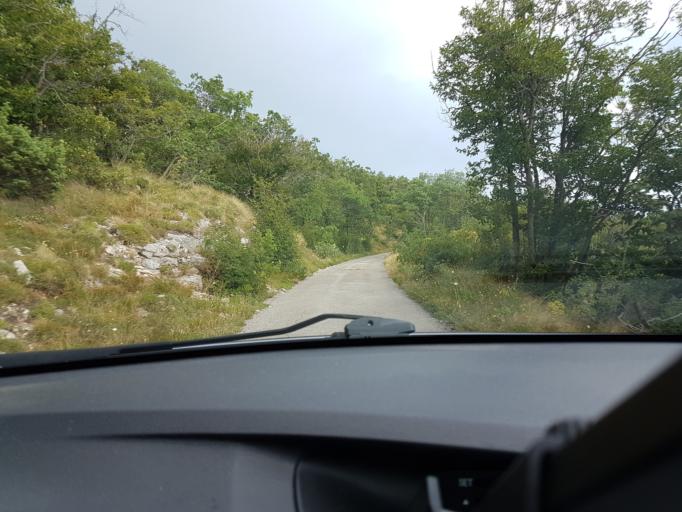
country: HR
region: Primorsko-Goranska
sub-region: Grad Crikvenica
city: Crikvenica
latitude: 45.2368
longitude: 14.6974
